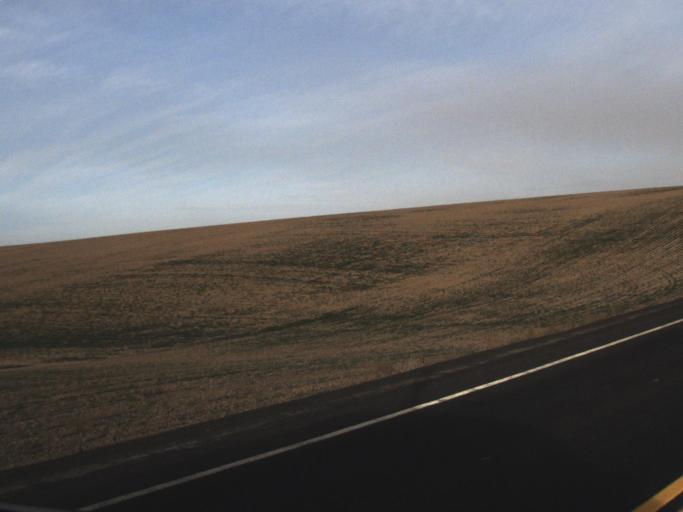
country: US
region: Washington
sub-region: Adams County
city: Ritzville
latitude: 47.1308
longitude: -118.6725
